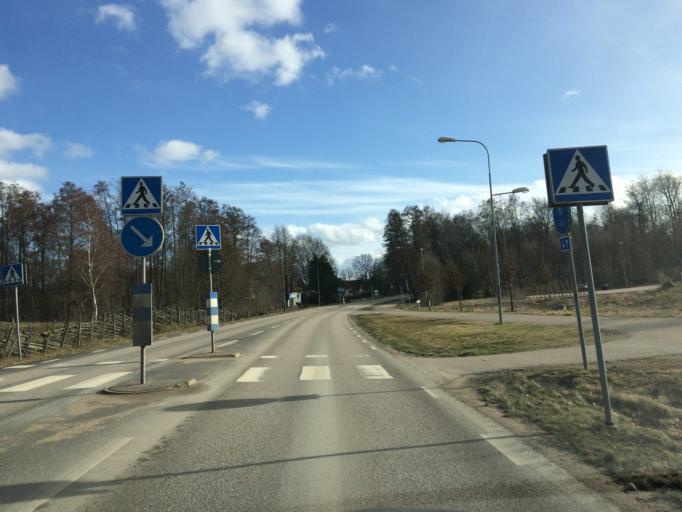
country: SE
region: Kronoberg
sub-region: Almhults Kommun
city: AElmhult
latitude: 56.5630
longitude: 14.1301
